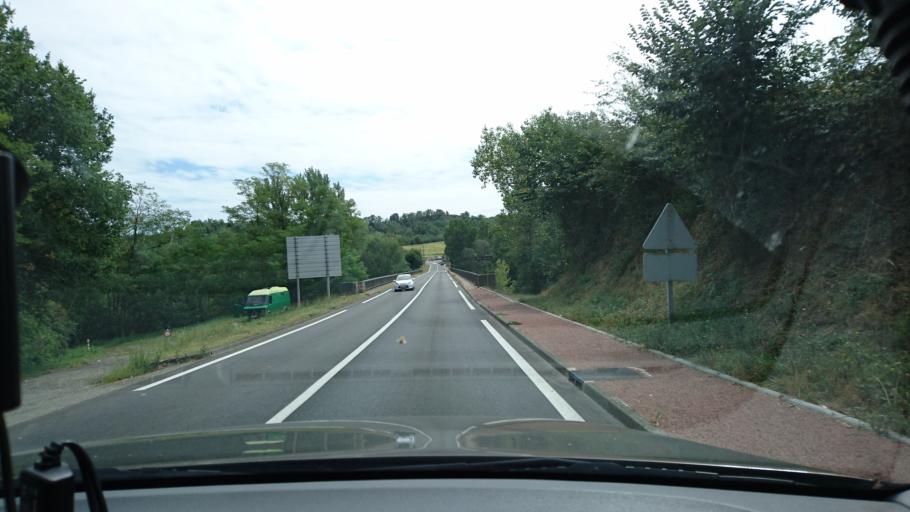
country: FR
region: Midi-Pyrenees
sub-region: Departement de la Haute-Garonne
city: Longages
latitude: 43.3395
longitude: 1.2580
